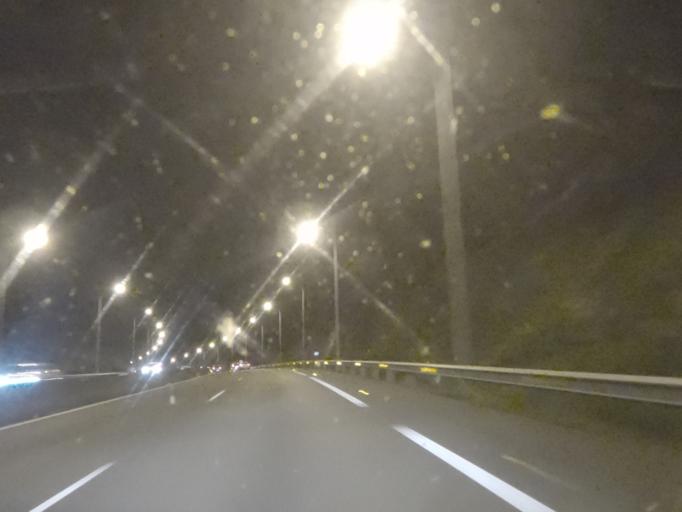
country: ES
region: Galicia
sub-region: Provincia da Coruna
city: Culleredo
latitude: 43.3215
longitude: -8.3926
